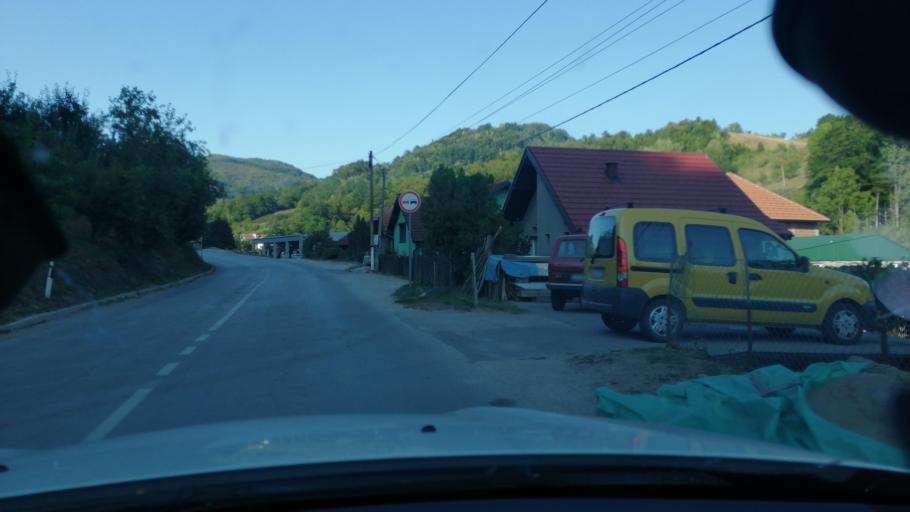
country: RS
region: Central Serbia
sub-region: Moravicki Okrug
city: Ivanjica
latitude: 43.6058
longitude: 20.2338
